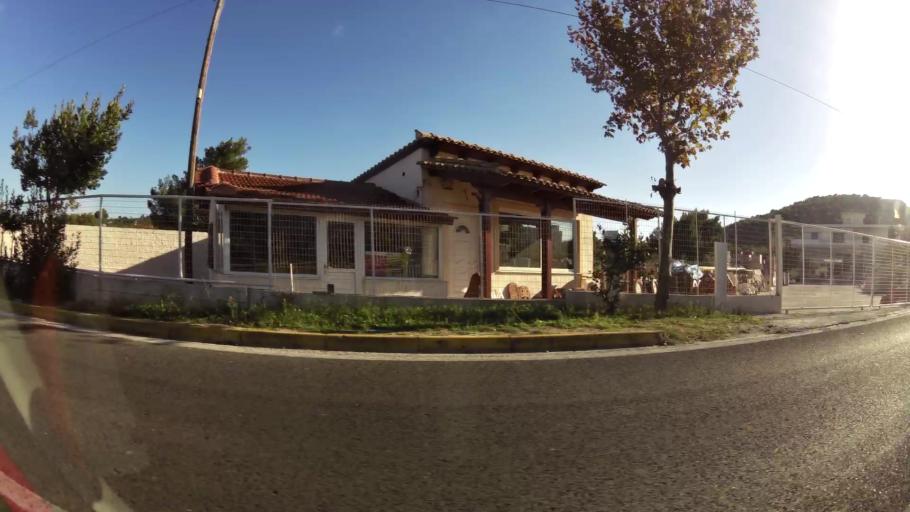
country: GR
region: Attica
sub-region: Nomarchia Anatolikis Attikis
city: Pikermi
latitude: 38.0081
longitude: 23.9648
